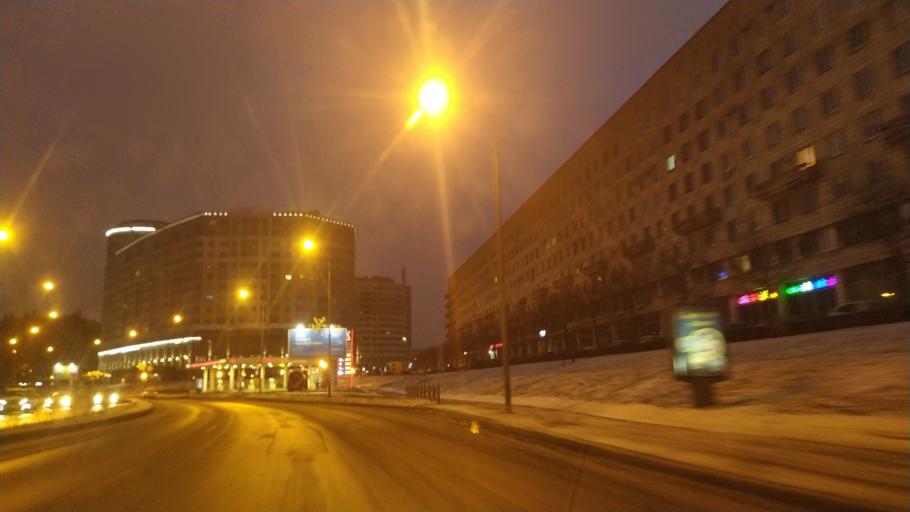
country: RU
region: Leningrad
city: Finlyandskiy
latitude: 59.9536
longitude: 30.4078
